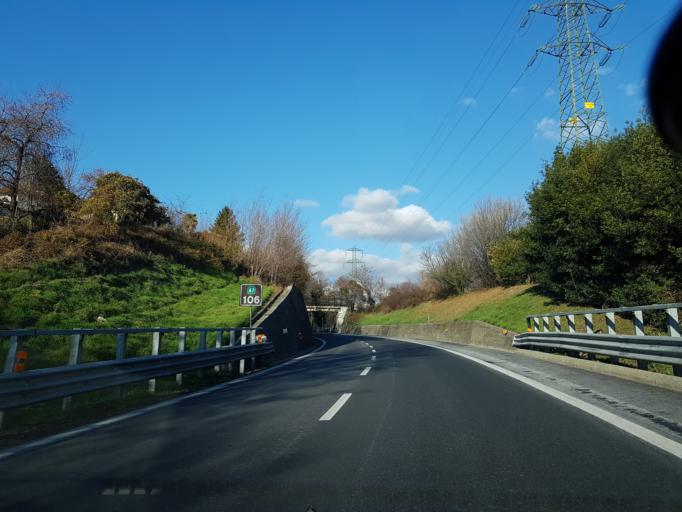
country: IT
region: Liguria
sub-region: Provincia di Genova
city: Pedemonte
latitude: 44.4922
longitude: 8.9179
